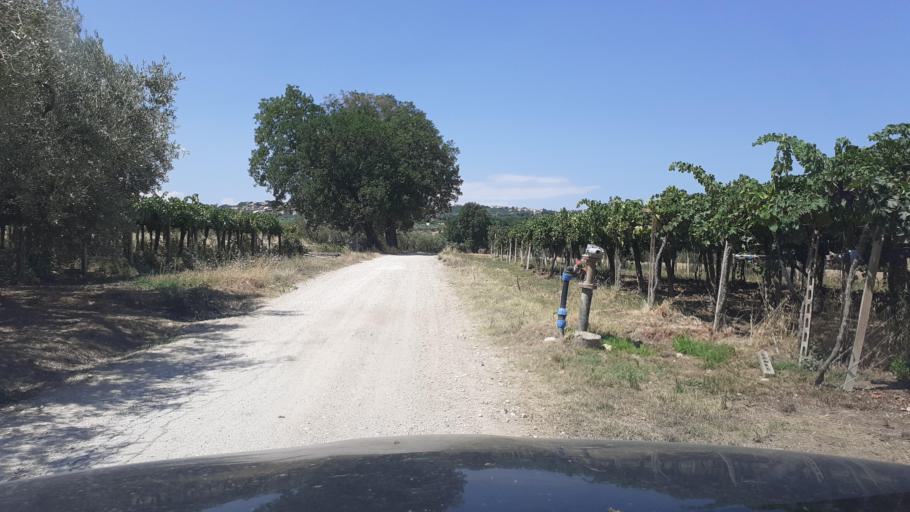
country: IT
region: Abruzzo
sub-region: Provincia di Chieti
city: Santa Maria Imbaro
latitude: 42.2069
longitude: 14.4792
